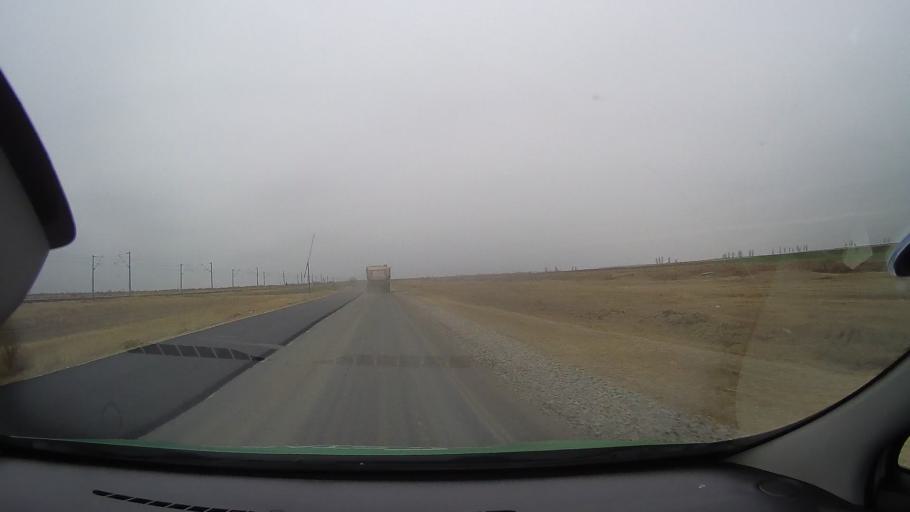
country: RO
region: Braila
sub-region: Comuna Baraganul
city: Baraganul
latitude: 44.7967
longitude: 27.5307
